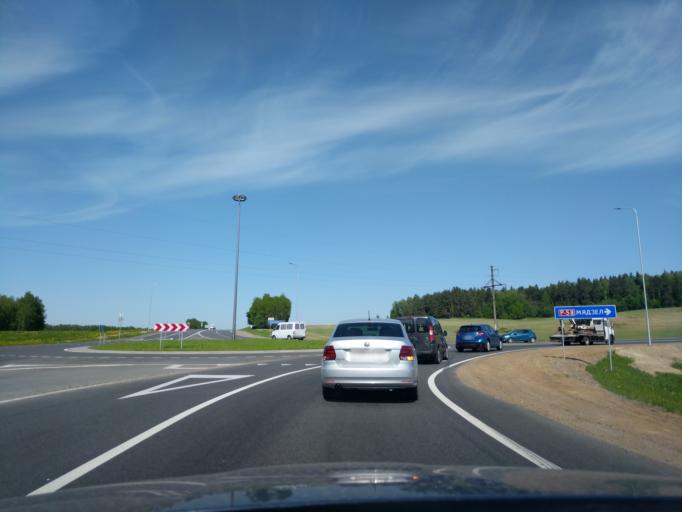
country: BY
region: Minsk
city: Bal'shavik
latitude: 54.0896
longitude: 27.5353
